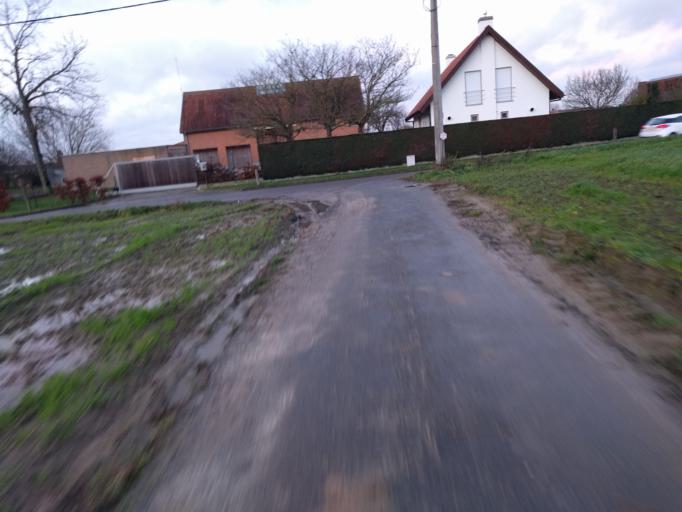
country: BE
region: Flanders
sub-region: Provincie West-Vlaanderen
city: Wevelgem
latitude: 50.8275
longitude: 3.1597
